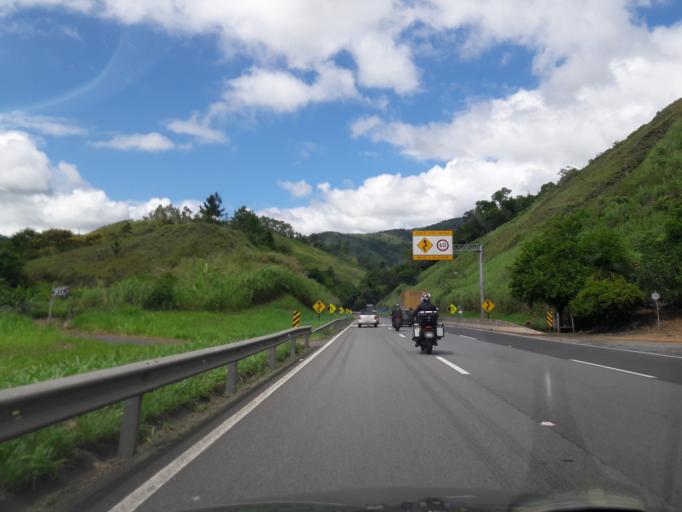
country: BR
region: Sao Paulo
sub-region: Cajati
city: Cajati
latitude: -24.8338
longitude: -48.2223
